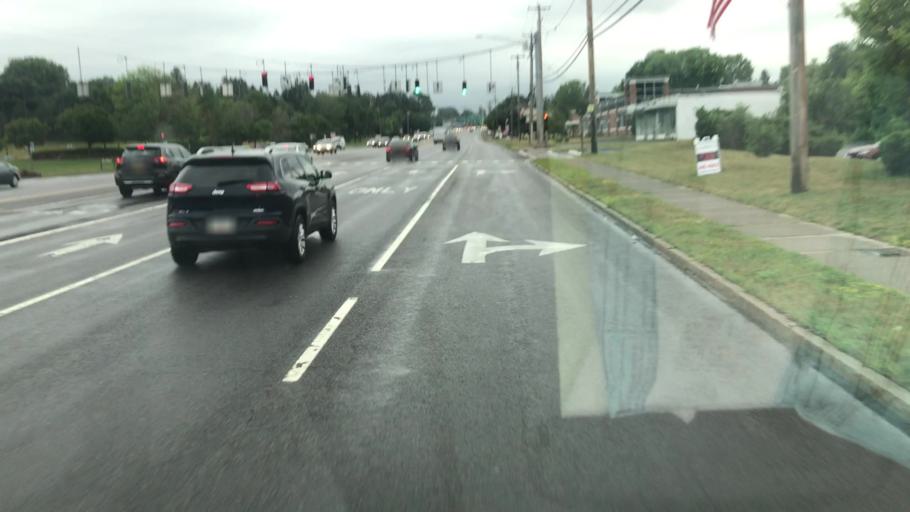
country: US
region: New York
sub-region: Onondaga County
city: East Syracuse
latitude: 43.0309
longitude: -76.0519
